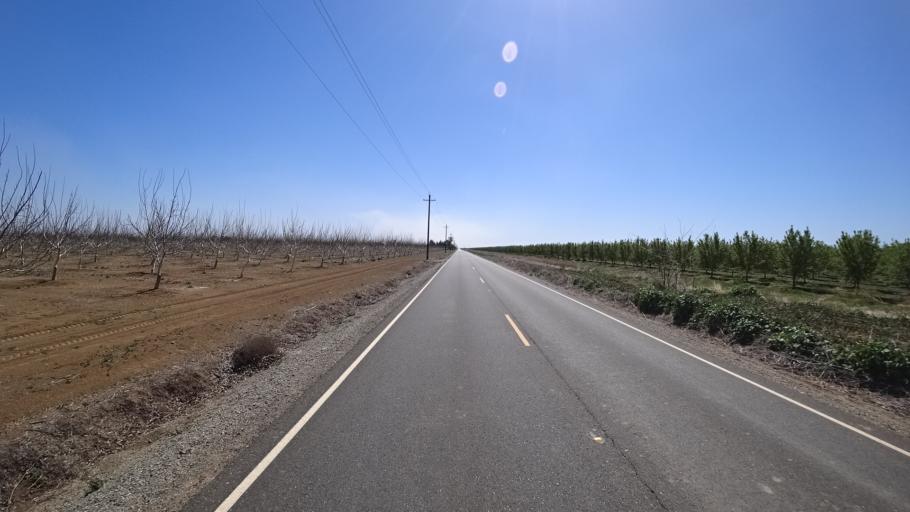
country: US
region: California
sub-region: Glenn County
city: Willows
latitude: 39.5046
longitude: -122.2491
